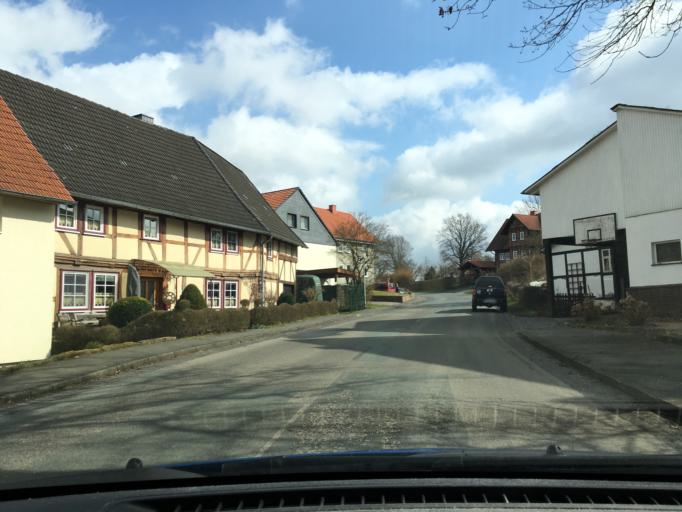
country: DE
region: Lower Saxony
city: Buhren
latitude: 51.5102
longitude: 9.6845
